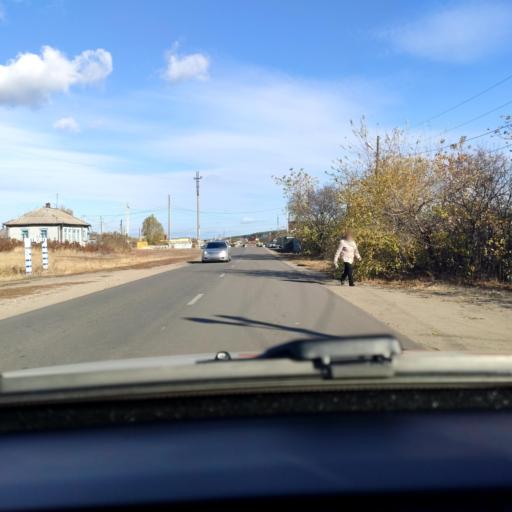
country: RU
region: Voronezj
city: Shilovo
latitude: 51.5265
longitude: 39.1514
